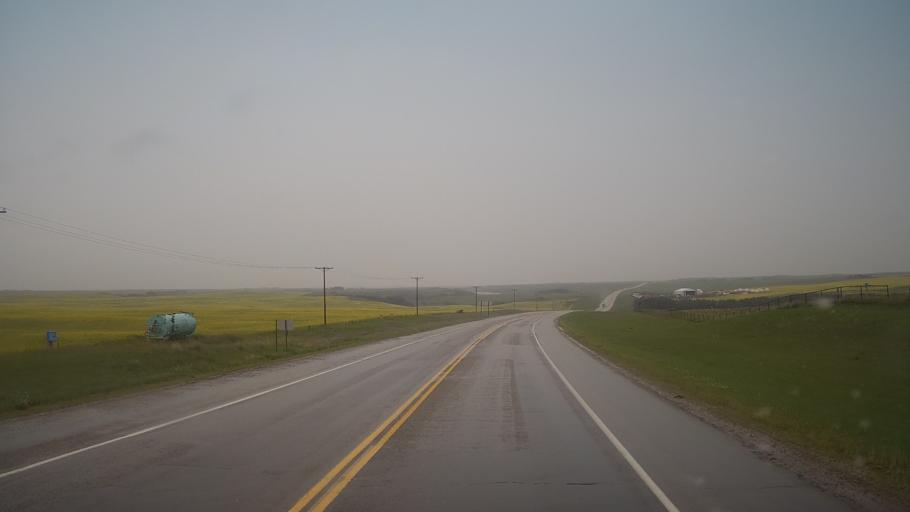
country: CA
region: Saskatchewan
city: Biggar
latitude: 52.0671
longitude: -108.0022
